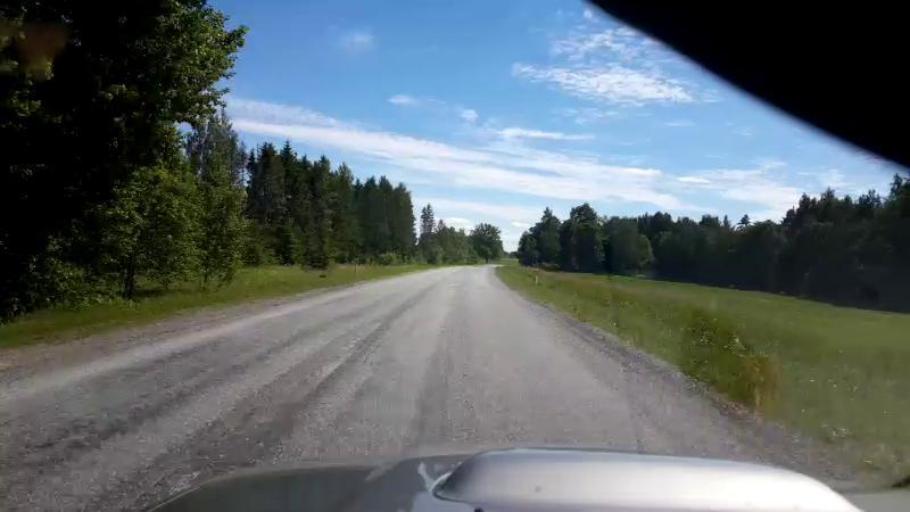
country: EE
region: Laeaene-Virumaa
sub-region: Rakke vald
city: Rakke
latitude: 58.8822
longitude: 26.2933
